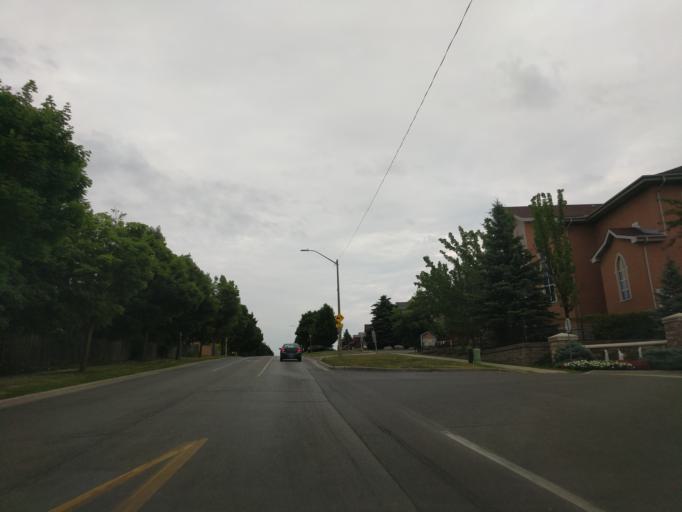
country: CA
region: Ontario
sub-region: York
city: Richmond Hill
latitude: 43.8666
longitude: -79.4236
